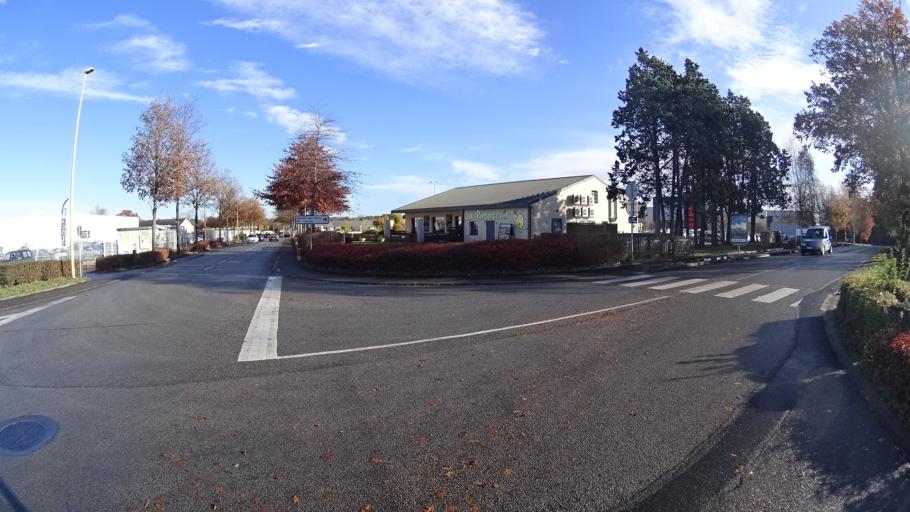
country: FR
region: Brittany
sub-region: Departement d'Ille-et-Vilaine
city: Redon
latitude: 47.6729
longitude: -2.0651
